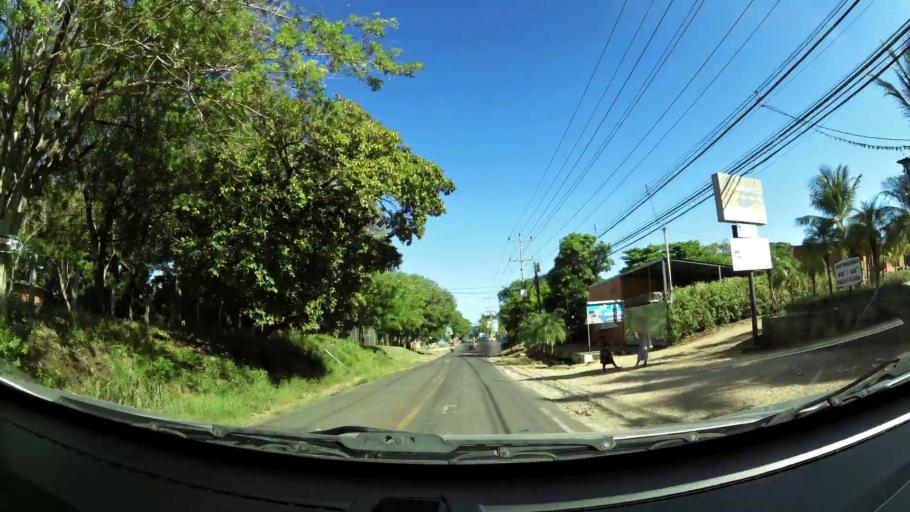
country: CR
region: Guanacaste
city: Sardinal
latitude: 10.4058
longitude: -85.7966
